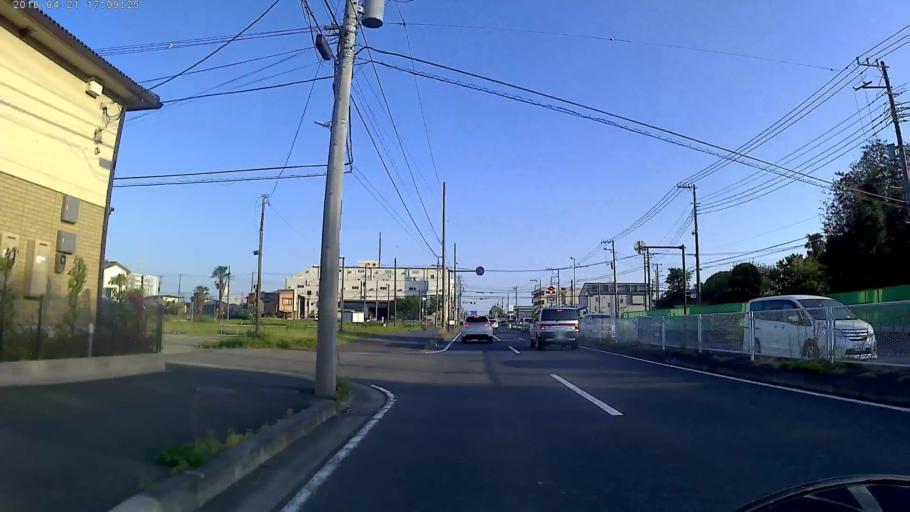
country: JP
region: Kanagawa
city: Fujisawa
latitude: 35.3971
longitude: 139.4429
